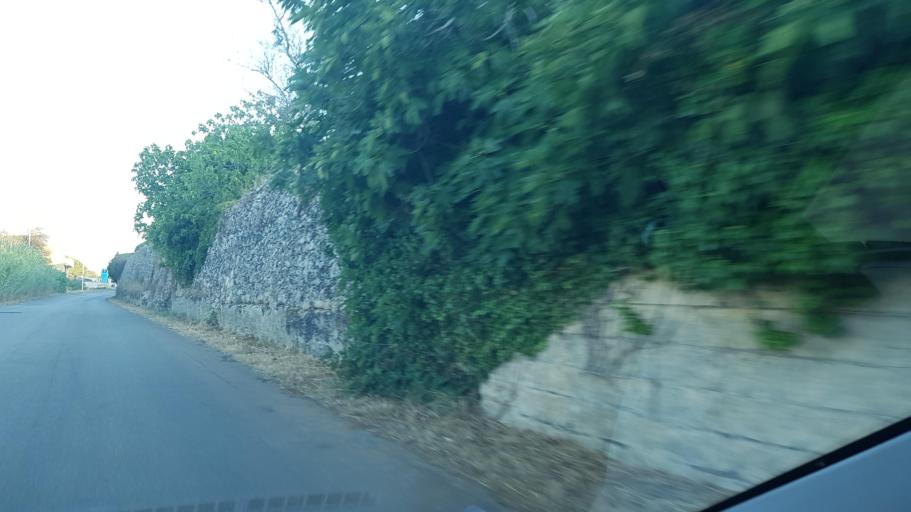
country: IT
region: Apulia
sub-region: Provincia di Lecce
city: Specchia
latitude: 39.9400
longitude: 18.3020
